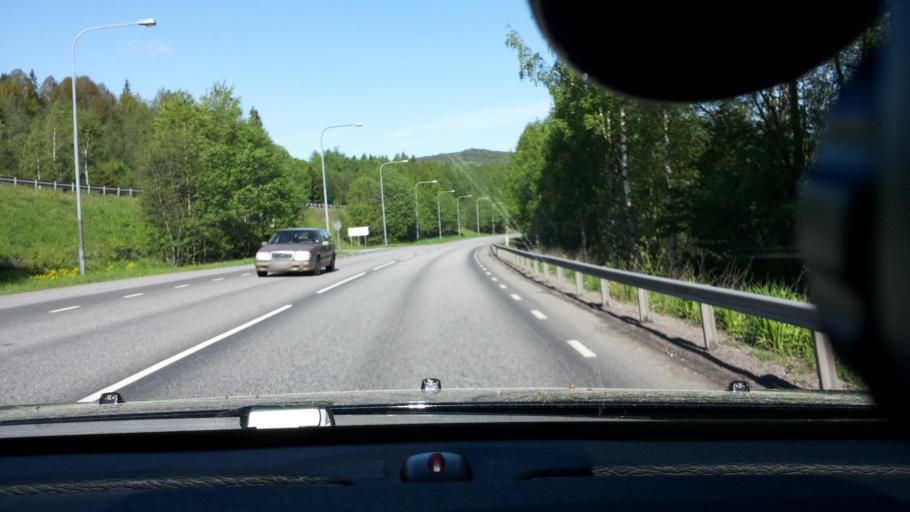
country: SE
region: Vaesternorrland
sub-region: Timra Kommun
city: Timra
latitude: 62.4673
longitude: 17.3251
